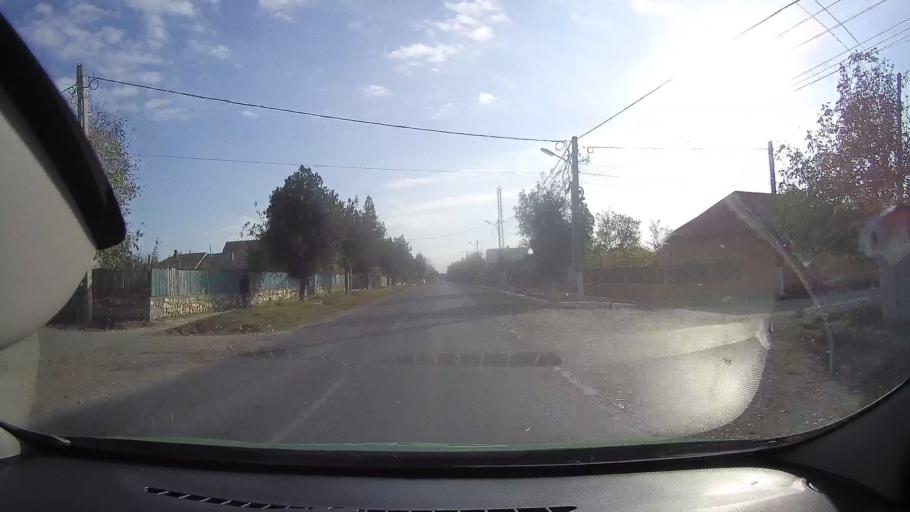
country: RO
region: Constanta
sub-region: Comuna Corbu
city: Corbu
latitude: 44.3863
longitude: 28.6622
